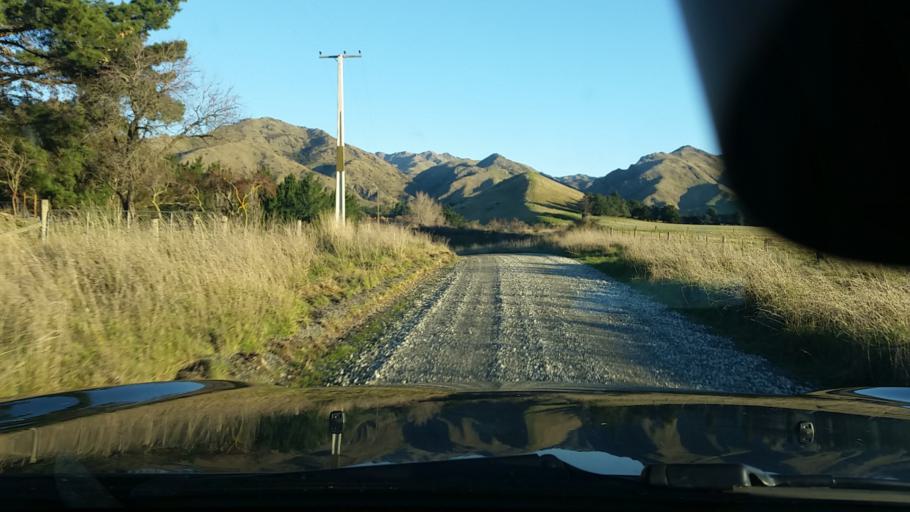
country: NZ
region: Marlborough
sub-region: Marlborough District
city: Blenheim
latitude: -41.7277
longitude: 174.0370
